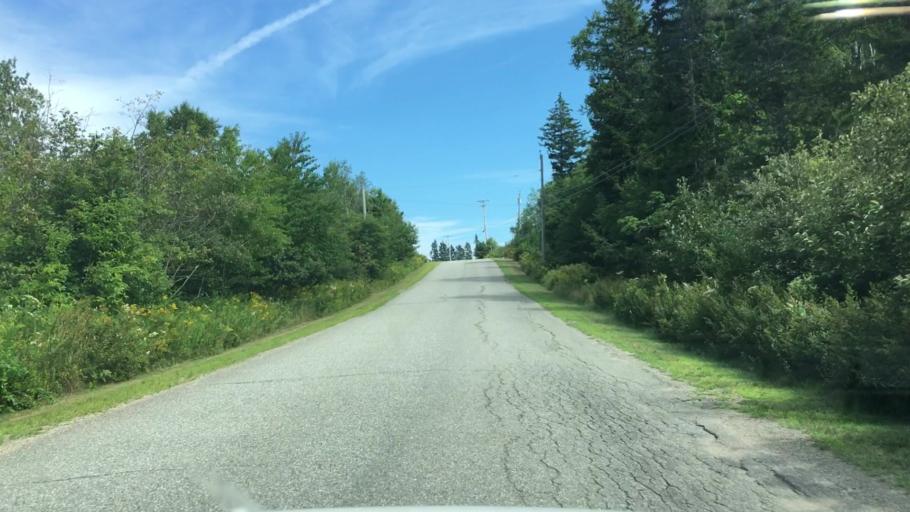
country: US
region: Maine
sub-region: Washington County
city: Eastport
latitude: 44.9274
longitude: -67.0310
